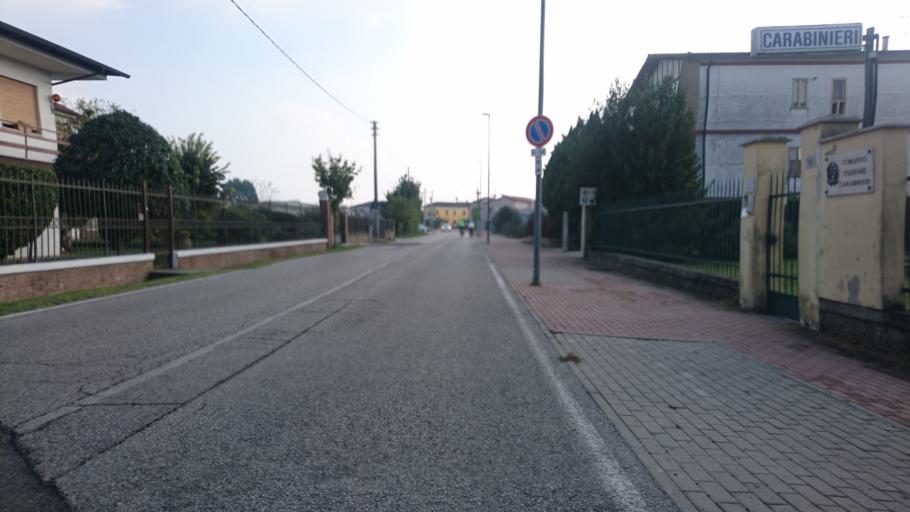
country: IT
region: Veneto
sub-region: Provincia di Rovigo
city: Arqua Polesine
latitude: 45.0057
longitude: 11.7414
